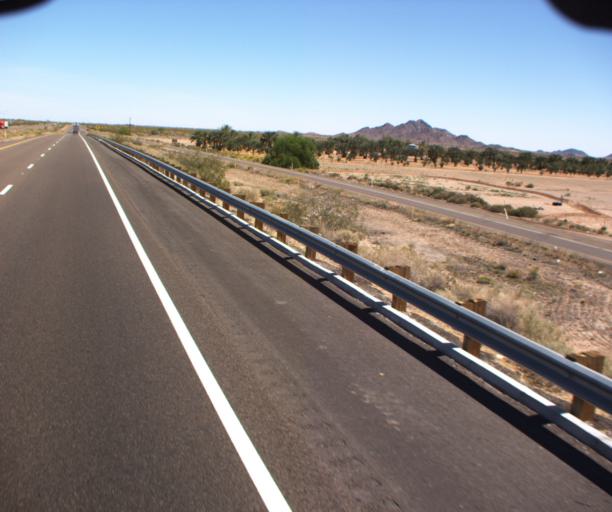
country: US
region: Arizona
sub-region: Yuma County
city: Wellton
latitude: 32.8005
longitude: -113.5407
